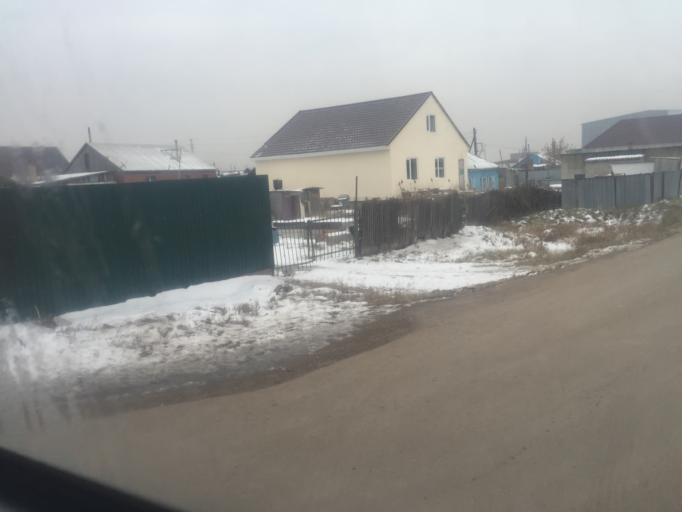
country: KZ
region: Astana Qalasy
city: Astana
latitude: 51.2086
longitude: 71.4051
